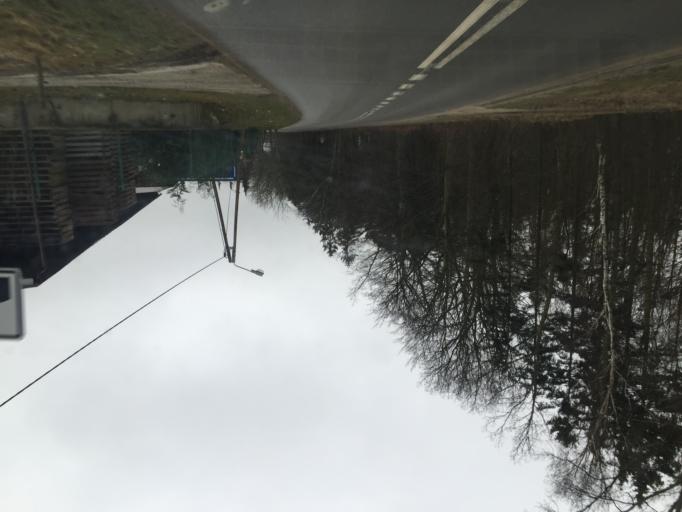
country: PL
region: Pomeranian Voivodeship
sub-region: Powiat kartuski
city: Banino
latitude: 54.3745
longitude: 18.4042
